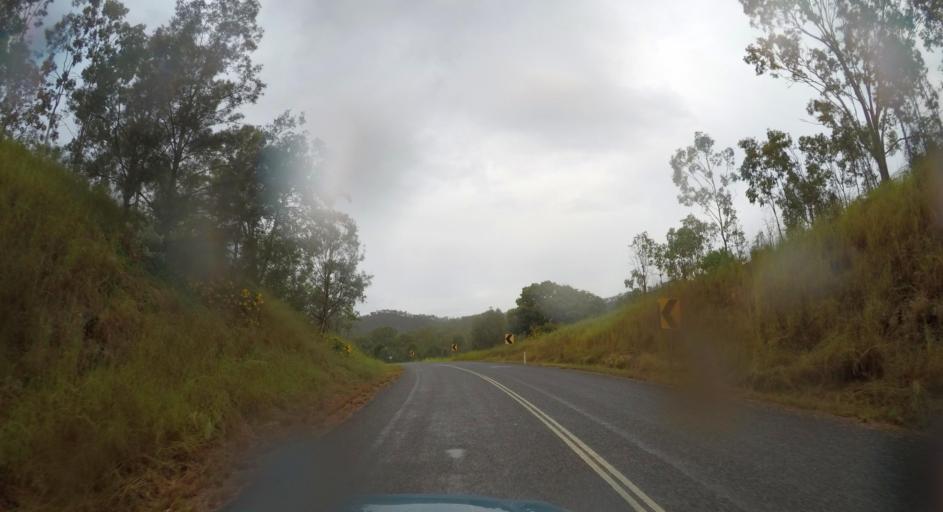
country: AU
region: Queensland
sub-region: Gladstone
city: Toolooa
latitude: -24.5457
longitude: 151.3652
